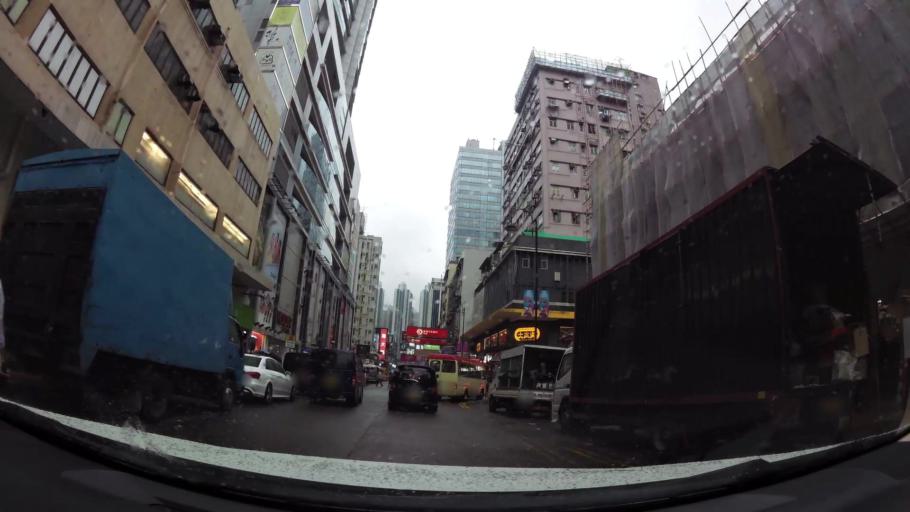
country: HK
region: Tsuen Wan
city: Tsuen Wan
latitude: 22.3711
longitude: 114.1177
